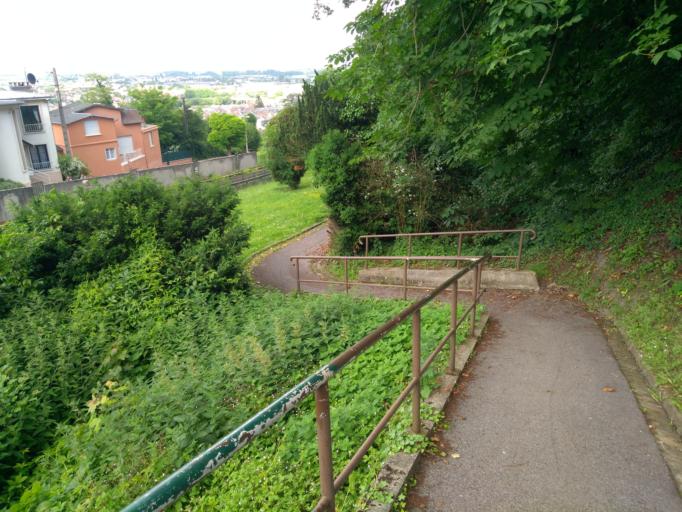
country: FR
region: Picardie
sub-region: Departement de l'Aisne
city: Laon
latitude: 49.5654
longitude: 3.6264
